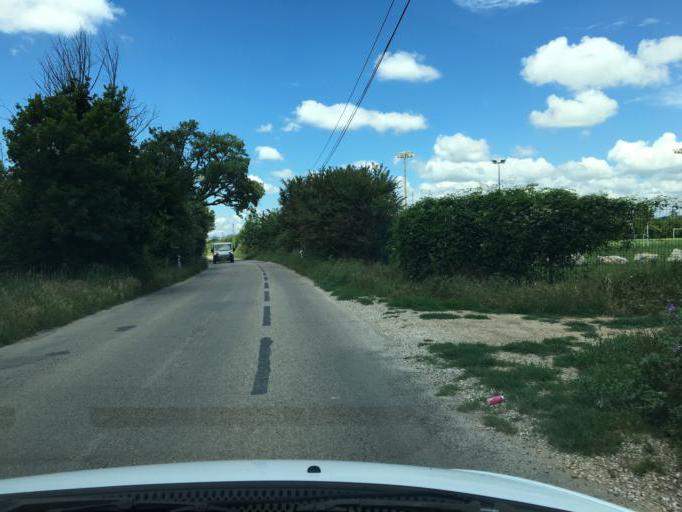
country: FR
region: Provence-Alpes-Cote d'Azur
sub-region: Departement du Vaucluse
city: Carpentras
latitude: 44.0397
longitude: 5.0559
